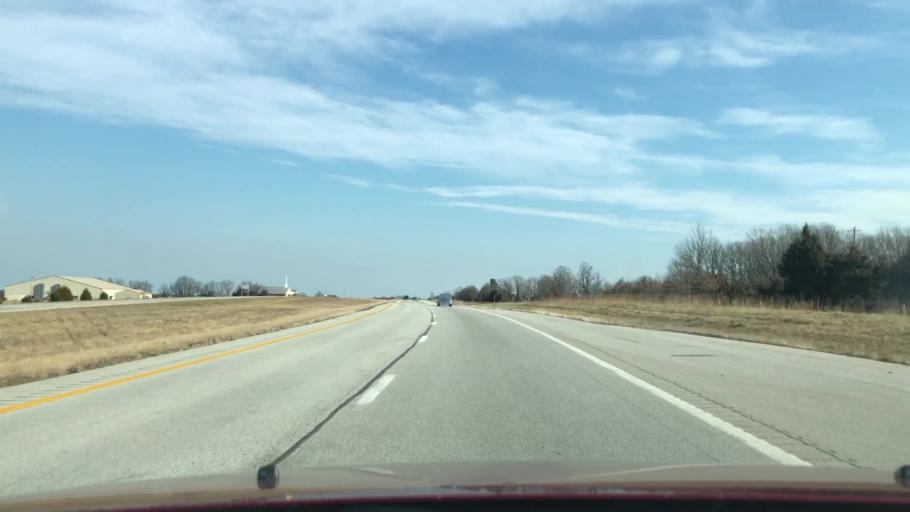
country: US
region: Missouri
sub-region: Webster County
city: Seymour
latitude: 37.1662
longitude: -92.8732
